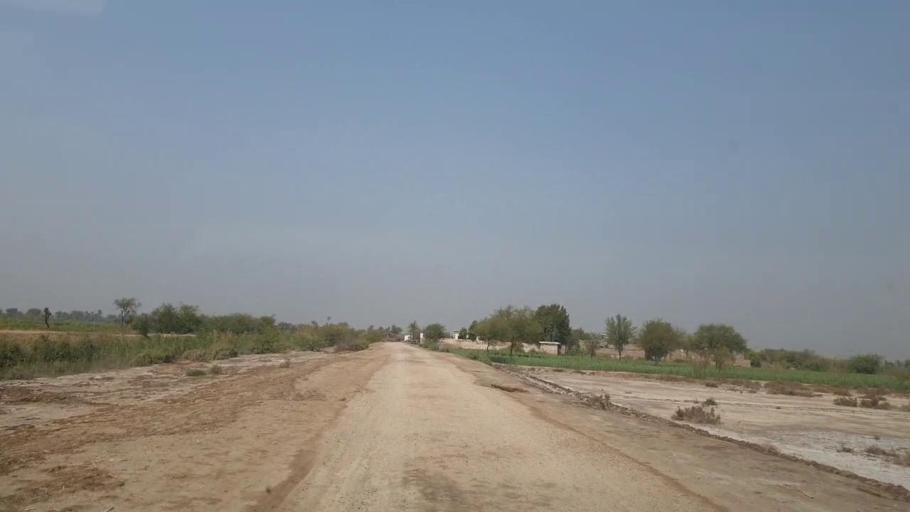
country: PK
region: Sindh
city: Mirpur Khas
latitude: 25.5510
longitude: 69.0766
